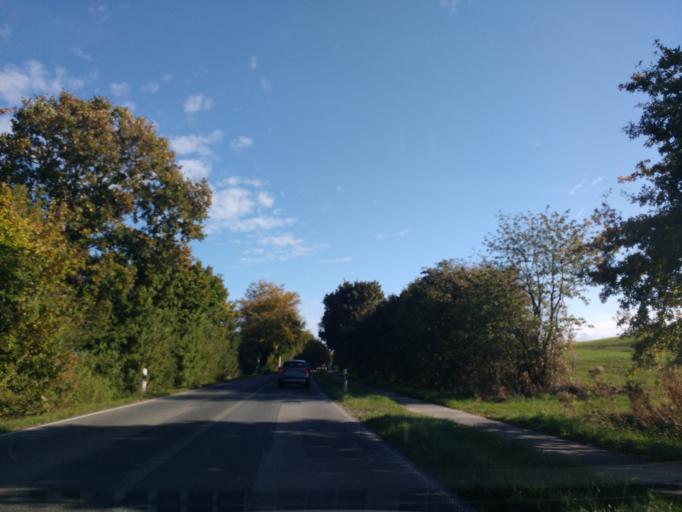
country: DE
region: Schleswig-Holstein
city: Timmendorfer Strand
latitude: 53.9658
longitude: 10.7622
